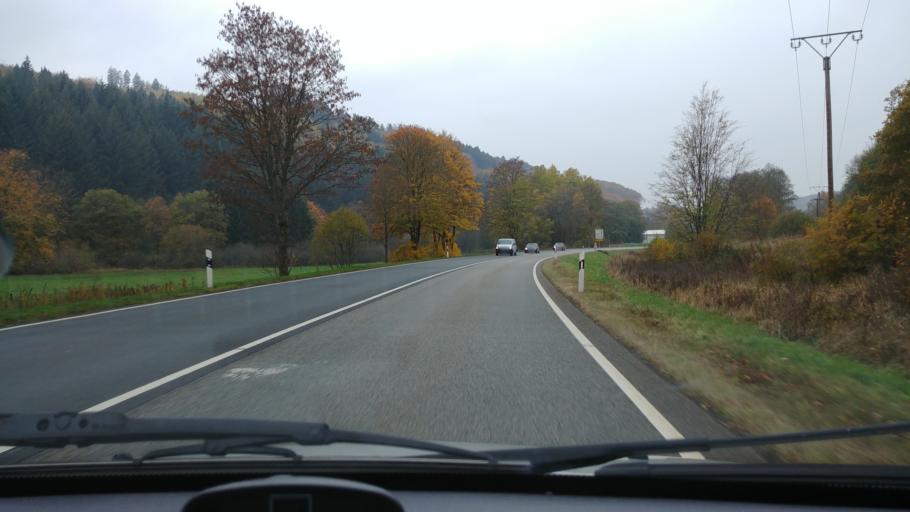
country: DE
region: Rheinland-Pfalz
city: Nauroth
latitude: 50.6672
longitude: 7.8692
